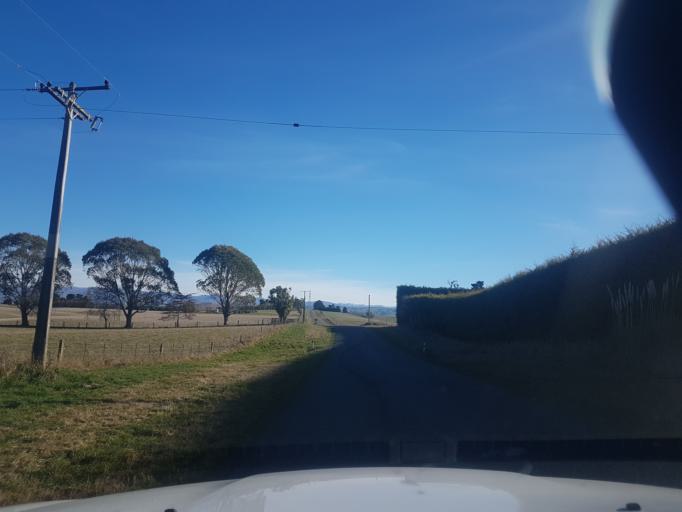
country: NZ
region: Canterbury
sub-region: Timaru District
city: Pleasant Point
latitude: -44.2522
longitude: 171.0514
